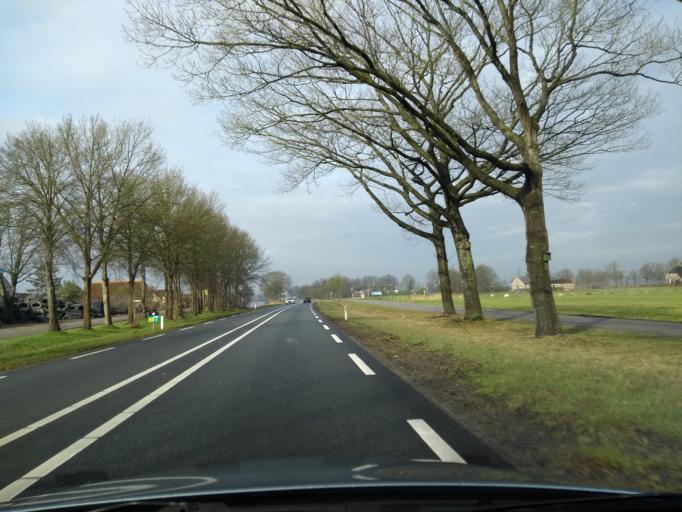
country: NL
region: Overijssel
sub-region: Gemeente Staphorst
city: Staphorst
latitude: 52.5920
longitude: 6.2600
